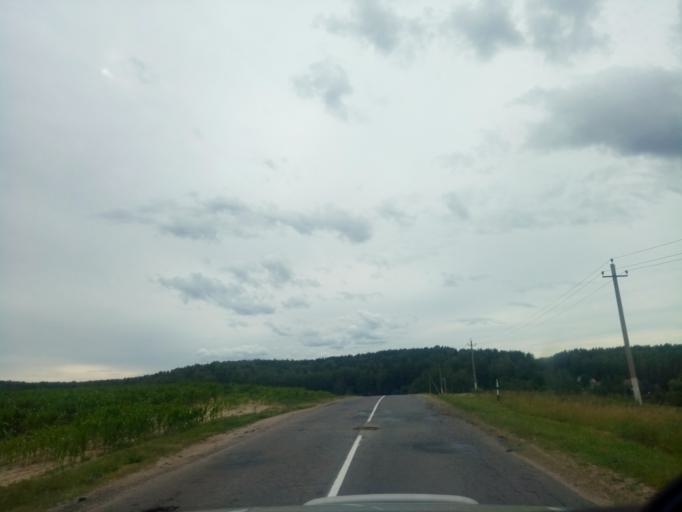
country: BY
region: Minsk
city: Zhdanovichy
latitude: 53.9361
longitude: 27.3956
